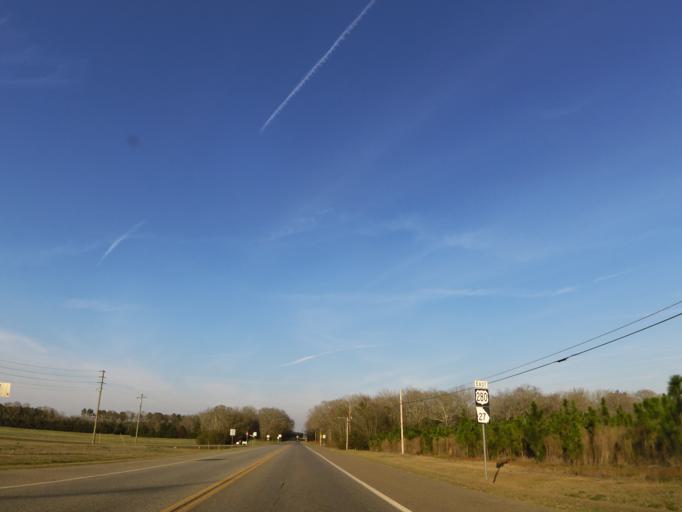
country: US
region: Georgia
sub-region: Webster County
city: Preston
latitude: 32.0369
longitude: -84.3882
